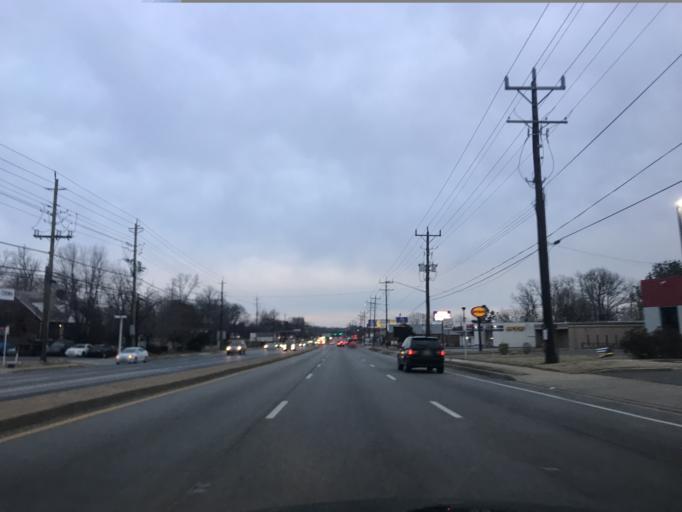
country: US
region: Maryland
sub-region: Prince George's County
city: Peppermill Village
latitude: 38.8898
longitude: -76.8621
